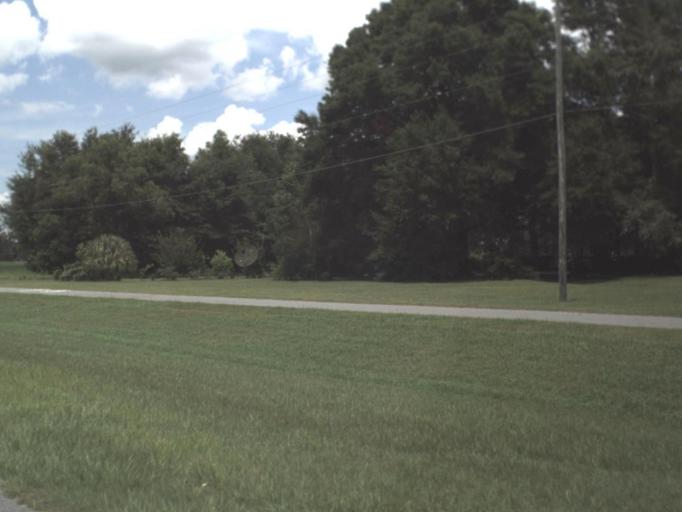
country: US
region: Florida
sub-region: Madison County
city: Madison
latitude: 30.5521
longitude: -83.3673
